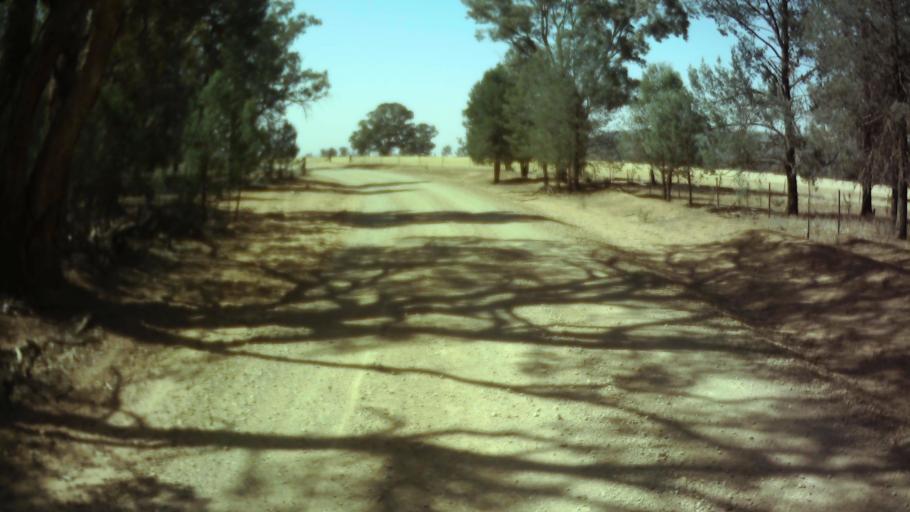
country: AU
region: New South Wales
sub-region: Weddin
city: Grenfell
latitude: -33.9596
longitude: 147.9321
